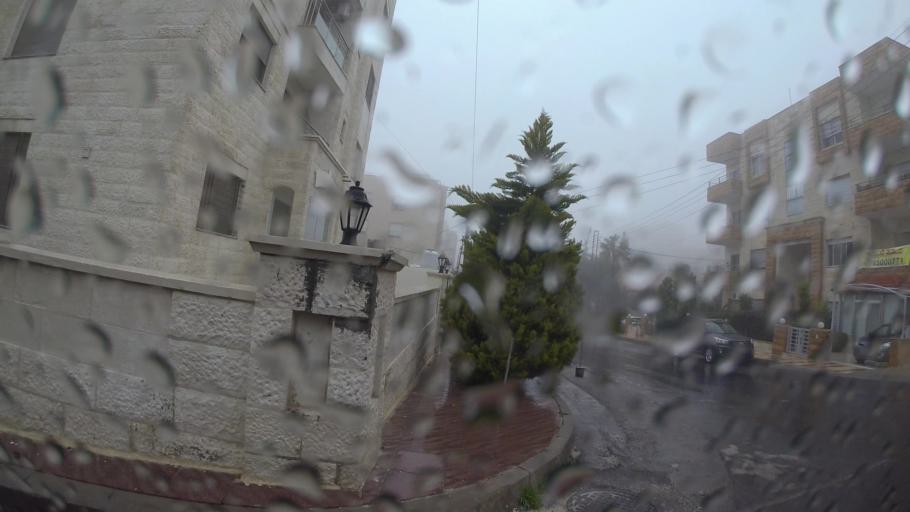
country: JO
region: Amman
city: Al Jubayhah
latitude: 32.0112
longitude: 35.8795
